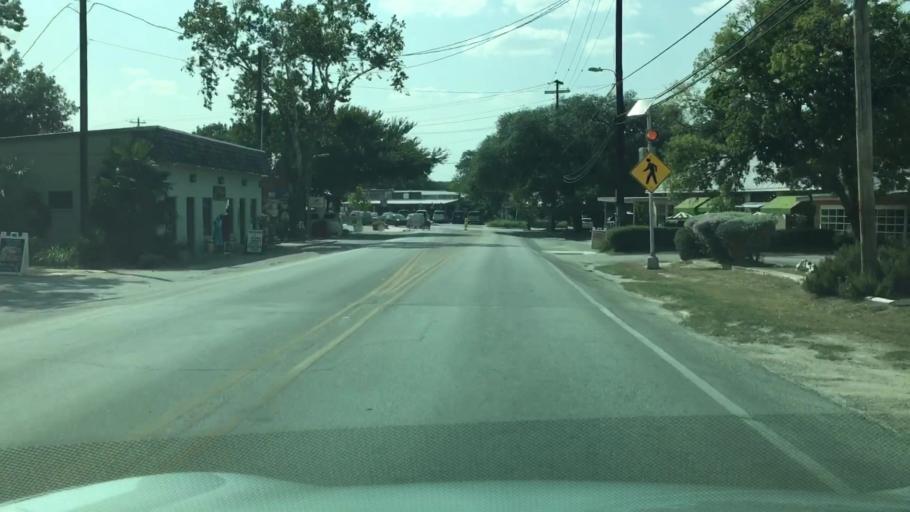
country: US
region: Texas
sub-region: Hays County
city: Wimberley
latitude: 29.9961
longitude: -98.0951
